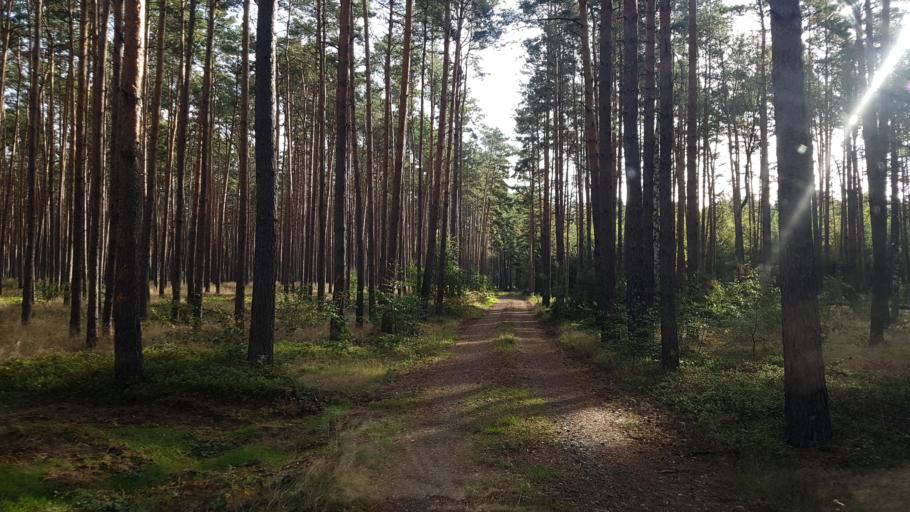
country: DE
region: Brandenburg
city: Hohenbucko
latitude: 51.8256
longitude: 13.5340
